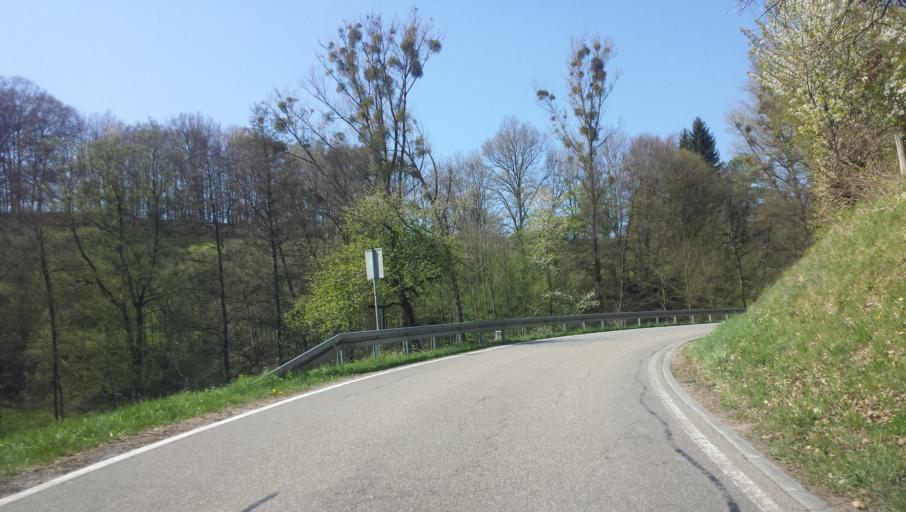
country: DE
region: Hesse
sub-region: Regierungsbezirk Darmstadt
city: Morlenbach
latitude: 49.6242
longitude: 8.7373
